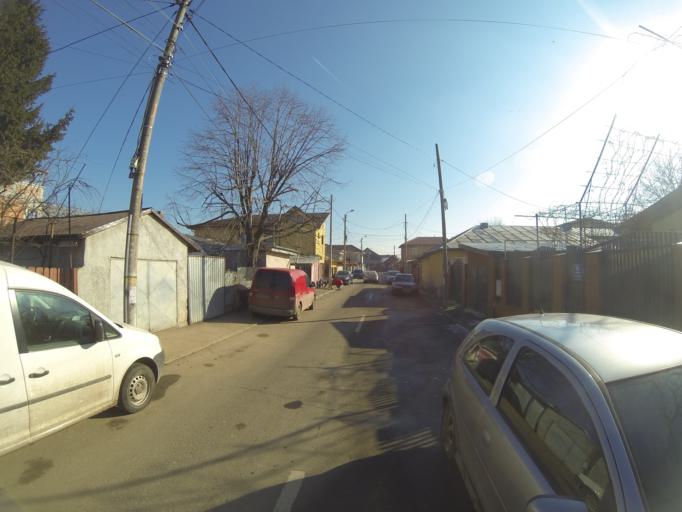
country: RO
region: Ilfov
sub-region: Comuna Magurele
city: Magurele
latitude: 44.3903
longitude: 26.0585
